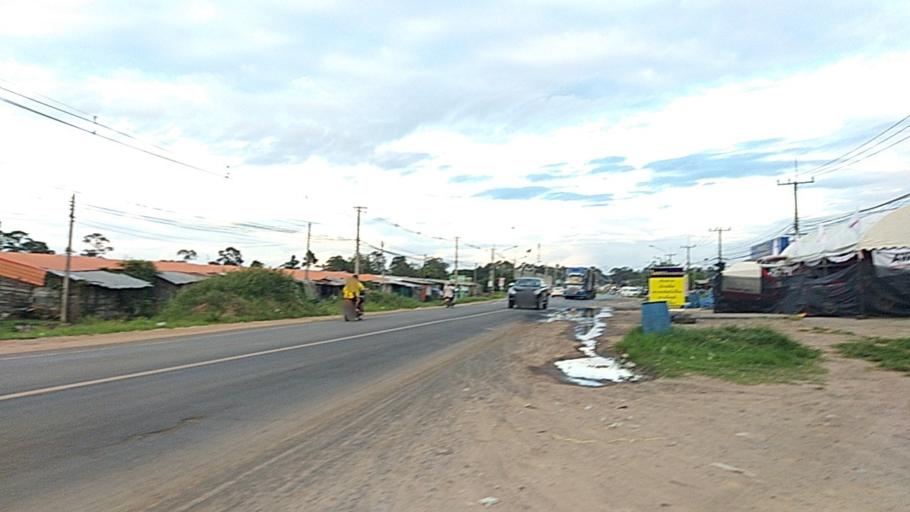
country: TH
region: Surin
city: Kap Choeng
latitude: 14.4542
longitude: 103.6863
